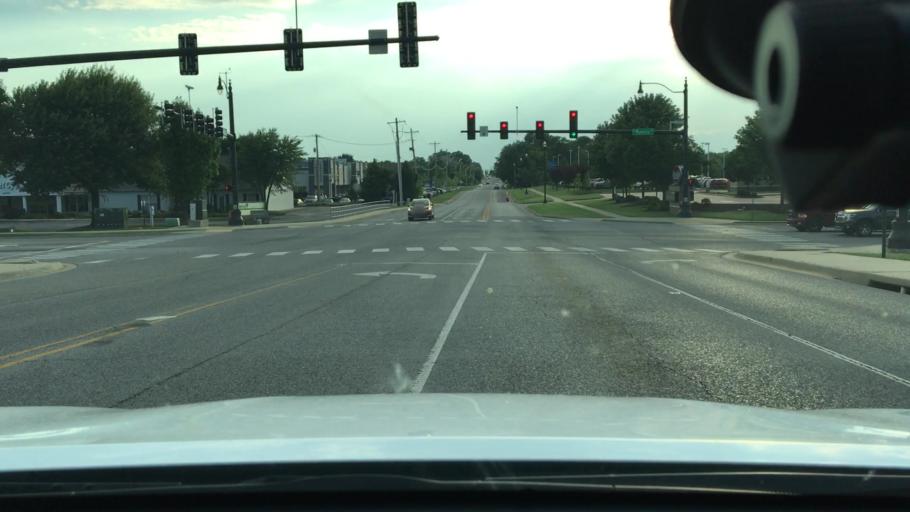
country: US
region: Arkansas
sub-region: Benton County
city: Bentonville
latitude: 36.3423
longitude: -94.1834
